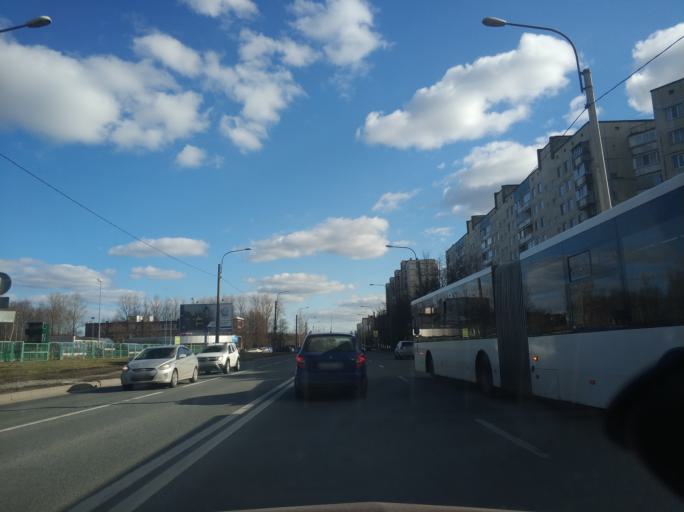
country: RU
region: St.-Petersburg
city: Krasnogvargeisky
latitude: 59.9567
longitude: 30.4941
